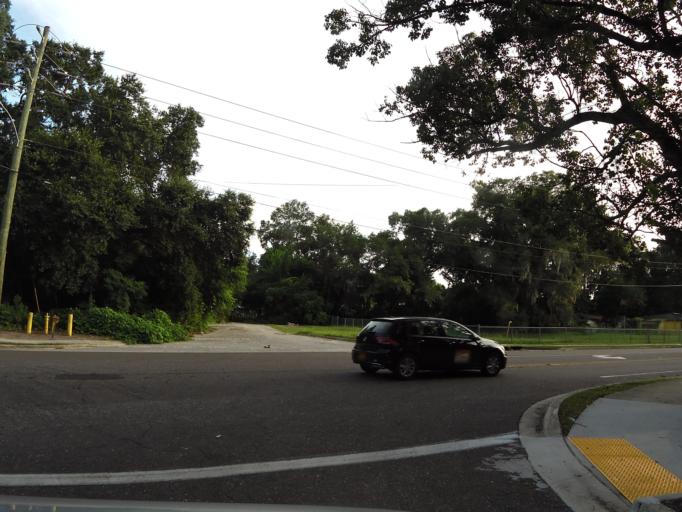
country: US
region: Florida
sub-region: Duval County
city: Jacksonville
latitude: 30.4299
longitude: -81.6902
